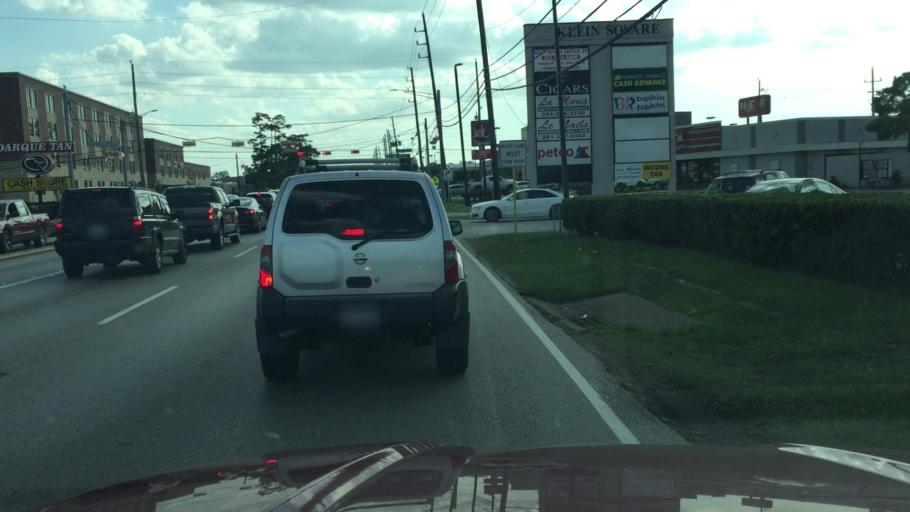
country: US
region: Texas
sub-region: Harris County
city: Tomball
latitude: 30.0216
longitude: -95.5230
